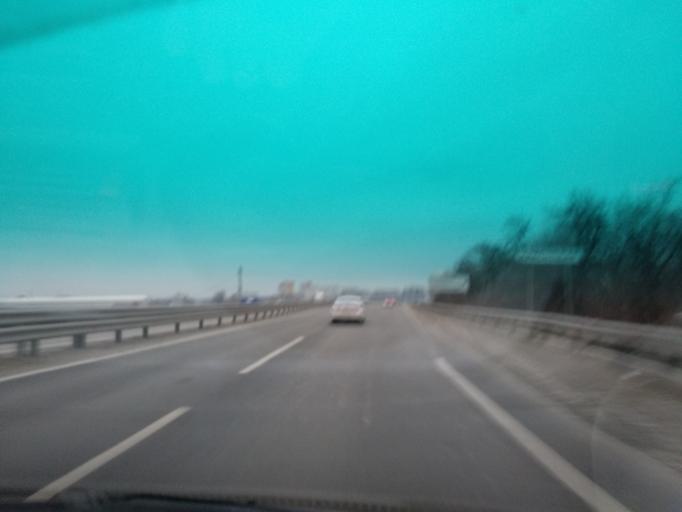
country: RU
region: Krasnodarskiy
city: Pashkovskiy
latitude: 45.0447
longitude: 39.1287
